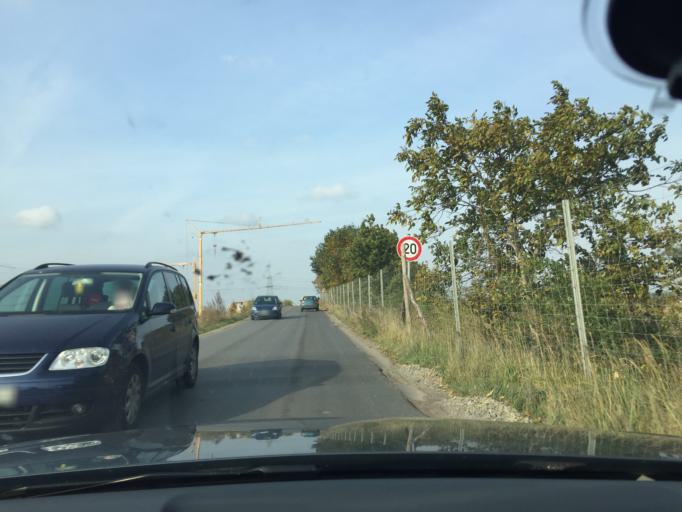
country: DE
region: Berlin
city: Buch
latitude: 52.6153
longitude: 13.5202
